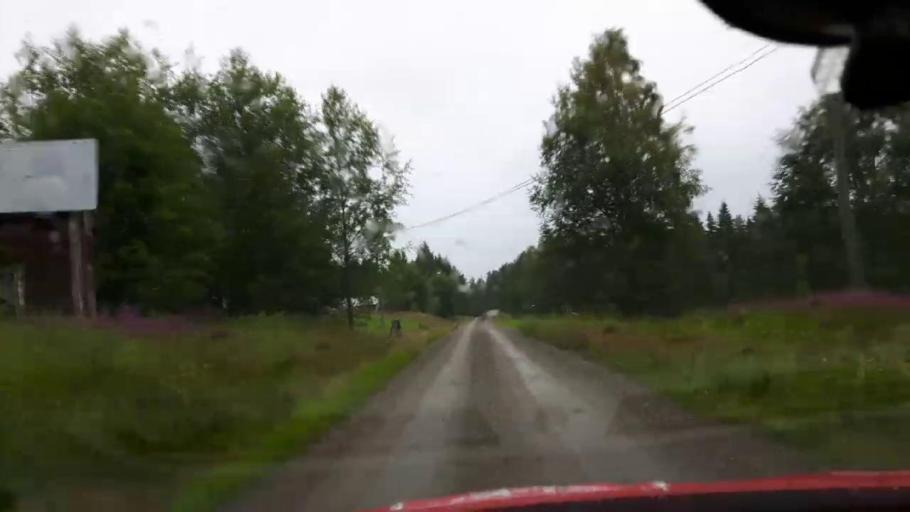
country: SE
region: Jaemtland
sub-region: OEstersunds Kommun
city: Brunflo
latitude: 62.7901
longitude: 14.9642
